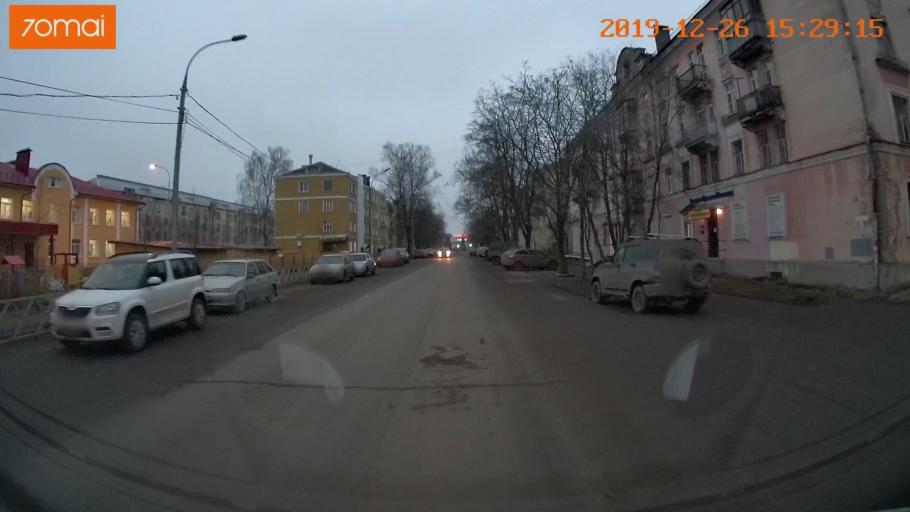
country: RU
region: Jaroslavl
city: Rybinsk
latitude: 58.0580
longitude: 38.8170
